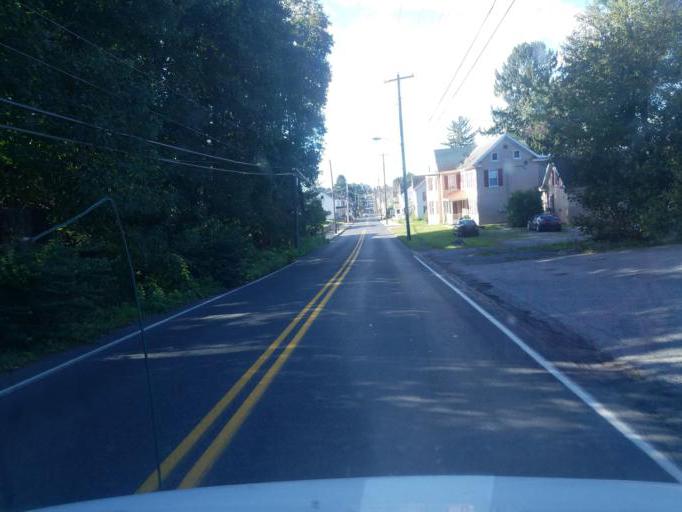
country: US
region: Pennsylvania
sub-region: Franklin County
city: Waynesboro
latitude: 39.7594
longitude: -77.5742
